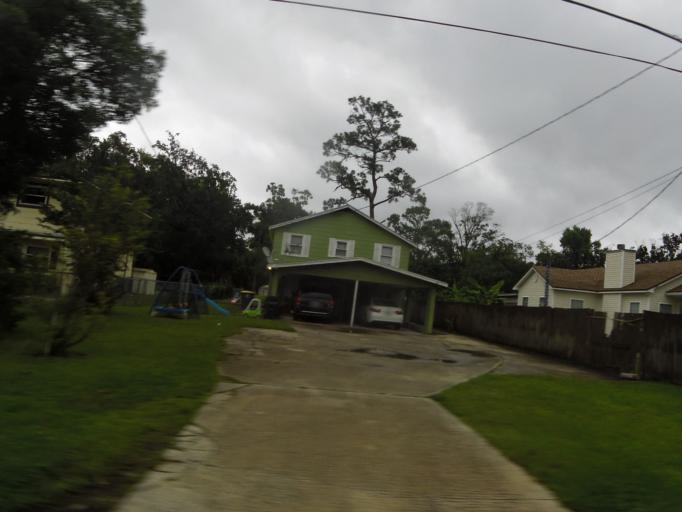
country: US
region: Florida
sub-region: Duval County
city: Jacksonville
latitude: 30.2795
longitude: -81.6228
